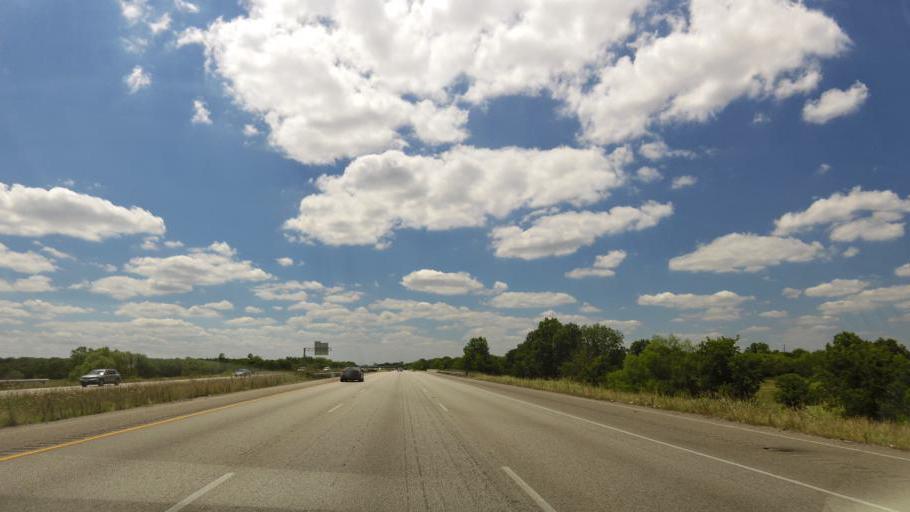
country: US
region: Texas
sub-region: Colorado County
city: Columbus
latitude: 29.6928
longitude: -96.5512
